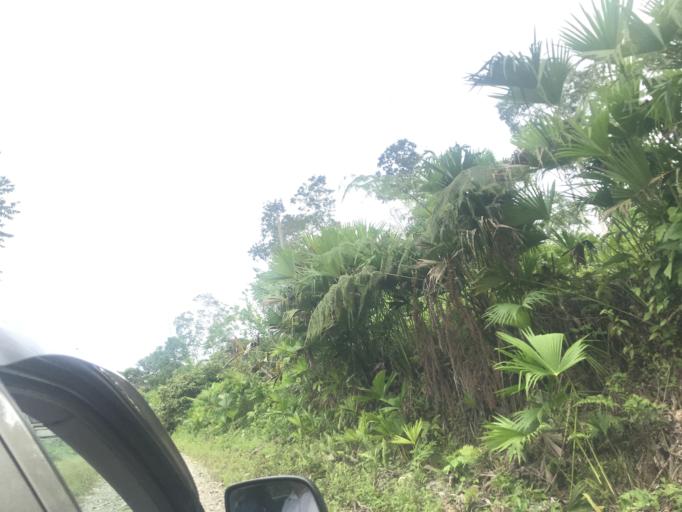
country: EC
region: Napo
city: Tena
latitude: -1.0189
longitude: -77.7427
